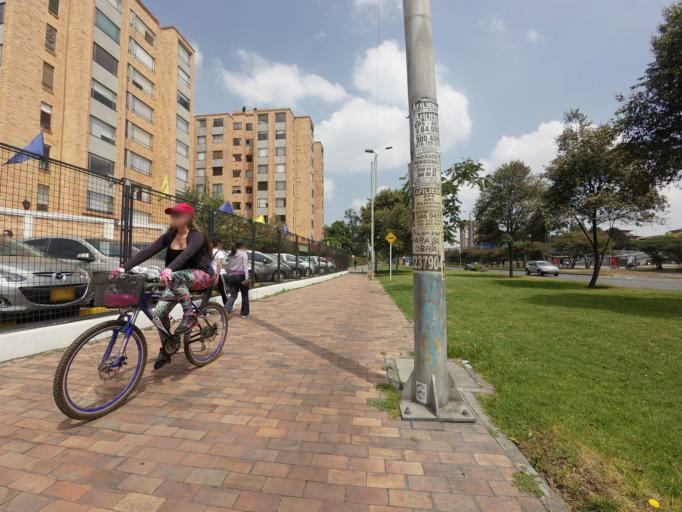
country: CO
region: Bogota D.C.
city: Barrio San Luis
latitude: 4.7179
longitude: -74.0758
